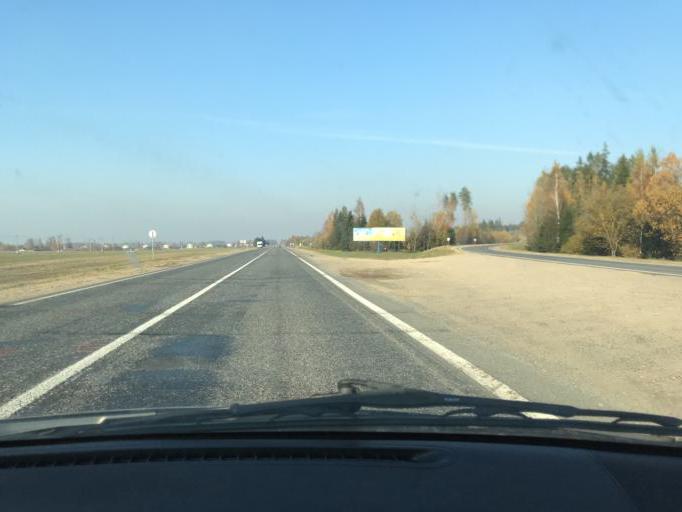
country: BY
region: Vitebsk
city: Orsha
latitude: 54.3960
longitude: 30.4431
